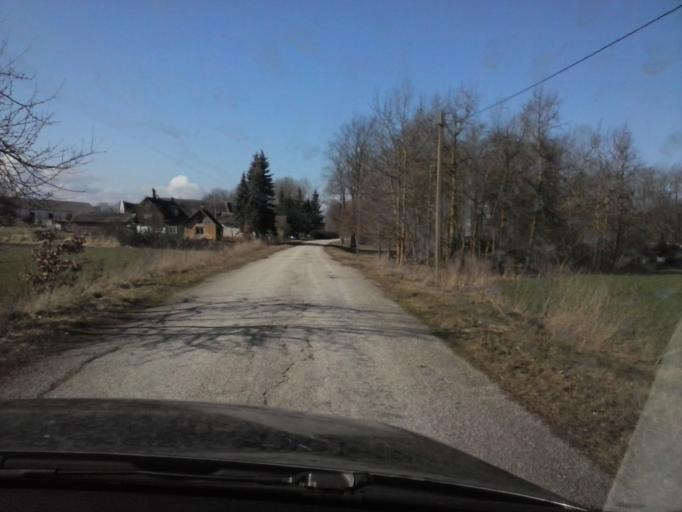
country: EE
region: Tartu
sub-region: Puhja vald
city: Puhja
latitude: 58.2834
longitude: 26.1696
